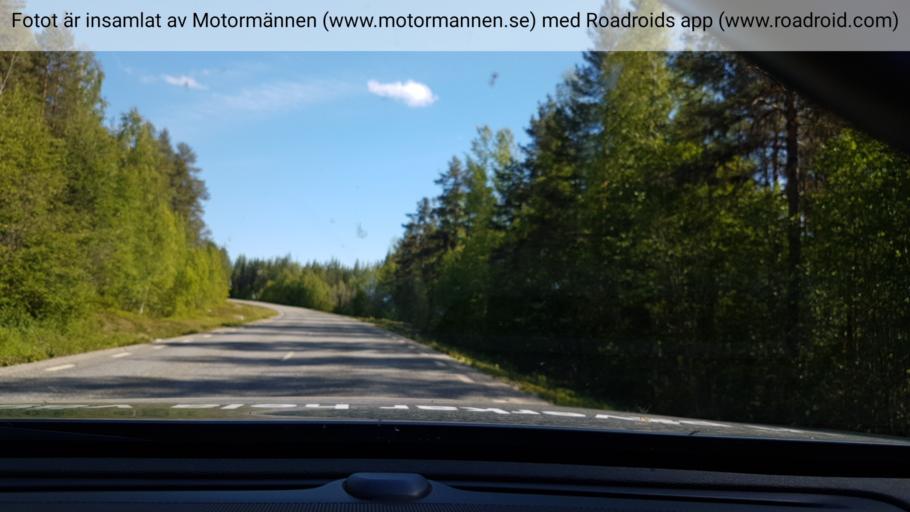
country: SE
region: Vaesterbotten
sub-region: Lycksele Kommun
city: Lycksele
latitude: 64.5860
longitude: 18.6116
